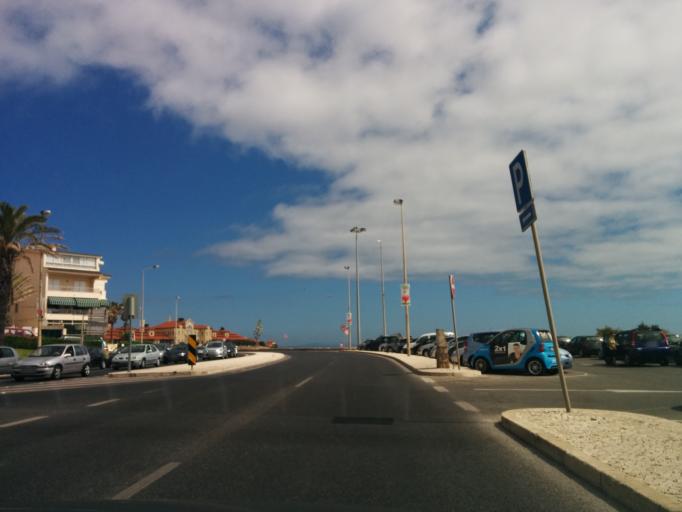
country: PT
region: Lisbon
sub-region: Cascais
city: Parede
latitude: 38.6854
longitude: -9.3525
